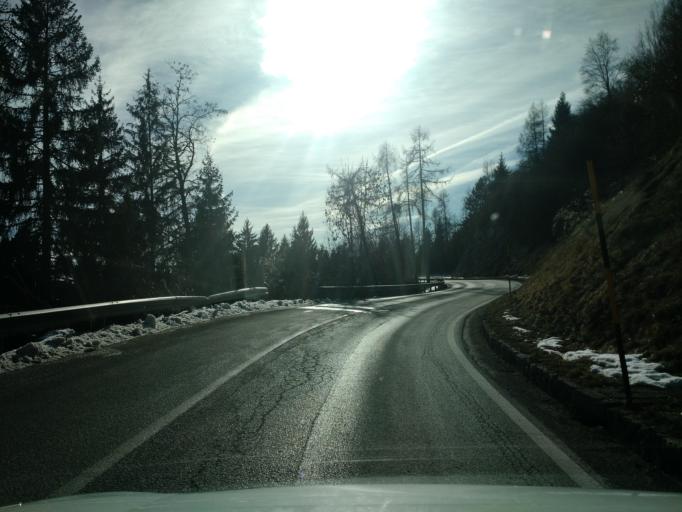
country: IT
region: Veneto
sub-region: Provincia di Vicenza
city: Canove di Roana
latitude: 45.8757
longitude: 11.4713
